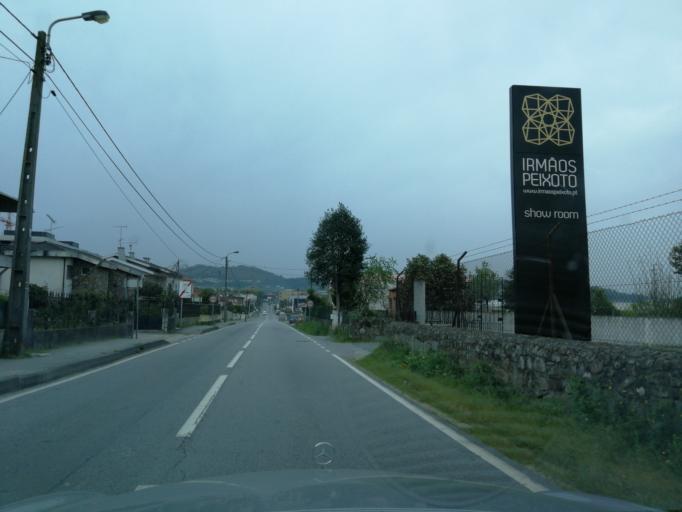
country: PT
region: Braga
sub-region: Braga
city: Braga
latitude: 41.5639
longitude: -8.4417
